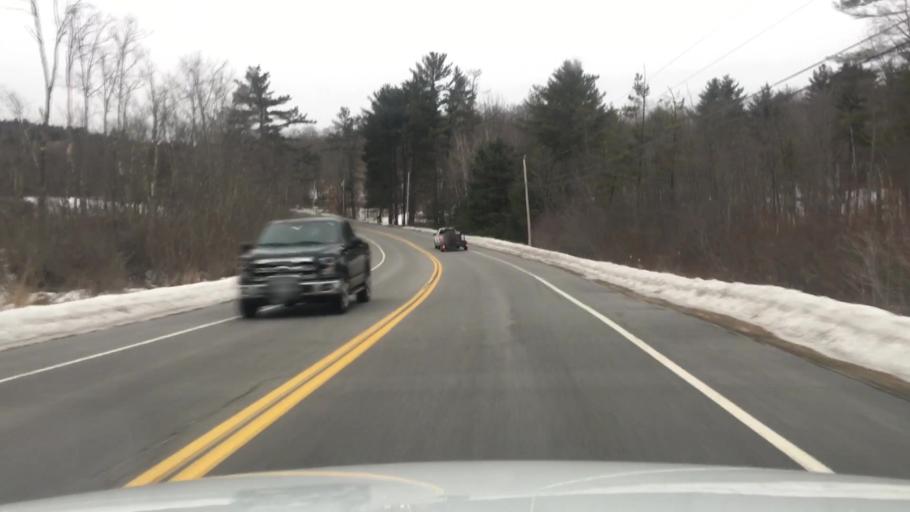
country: US
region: Maine
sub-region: York County
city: Limerick
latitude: 43.7318
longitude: -70.8157
